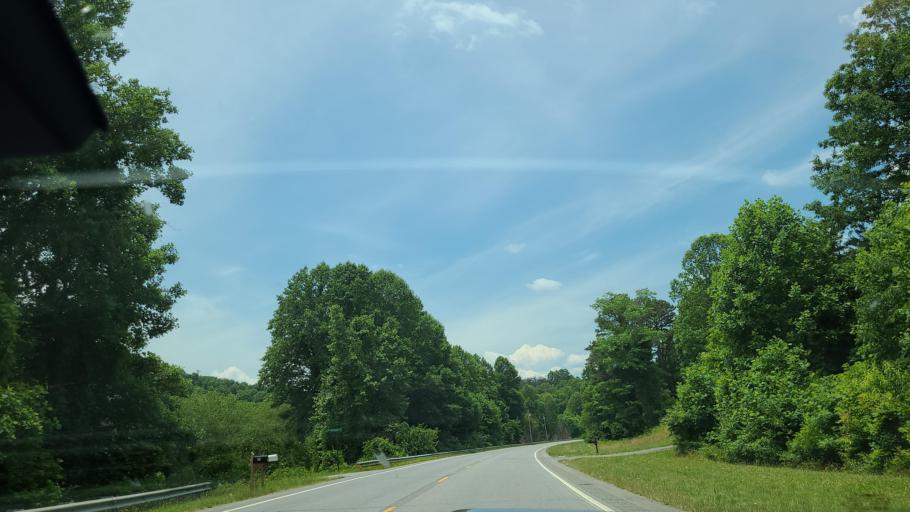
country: US
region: Georgia
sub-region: Towns County
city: Hiawassee
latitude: 35.0227
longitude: -83.6904
